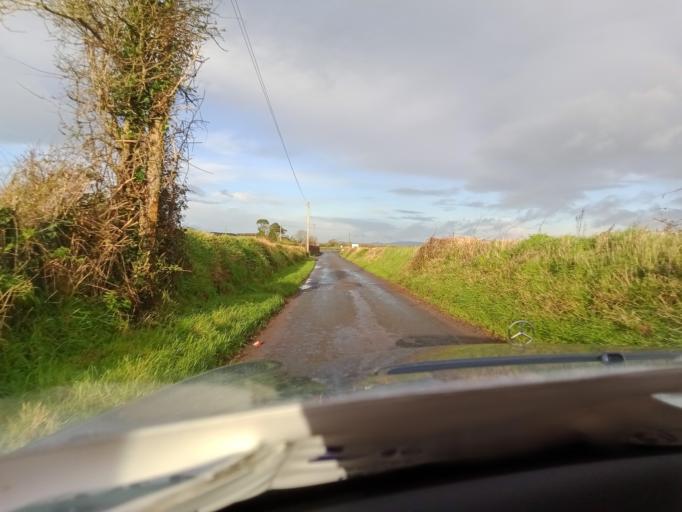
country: IE
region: Leinster
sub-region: Kilkenny
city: Mooncoin
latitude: 52.2810
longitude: -7.1979
